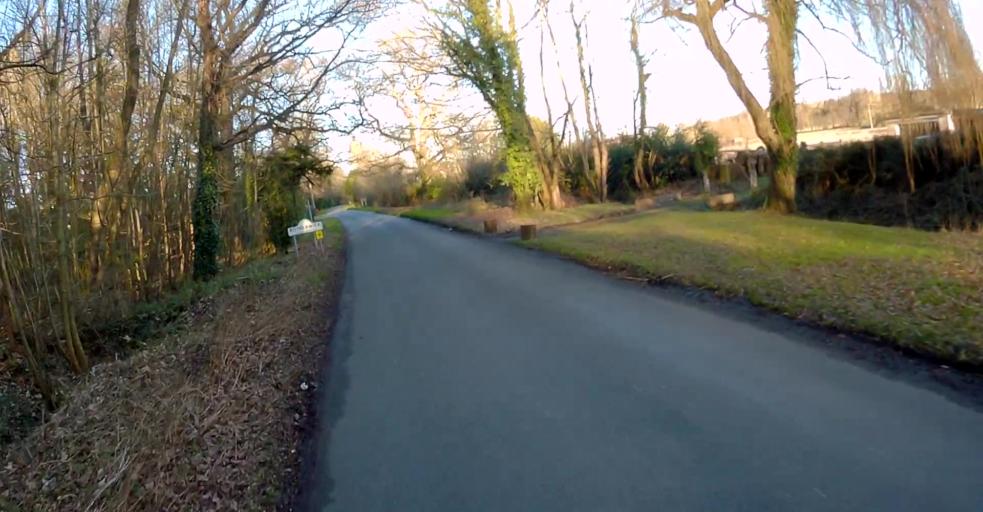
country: GB
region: England
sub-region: Hampshire
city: Hook
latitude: 51.2893
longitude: -0.9800
